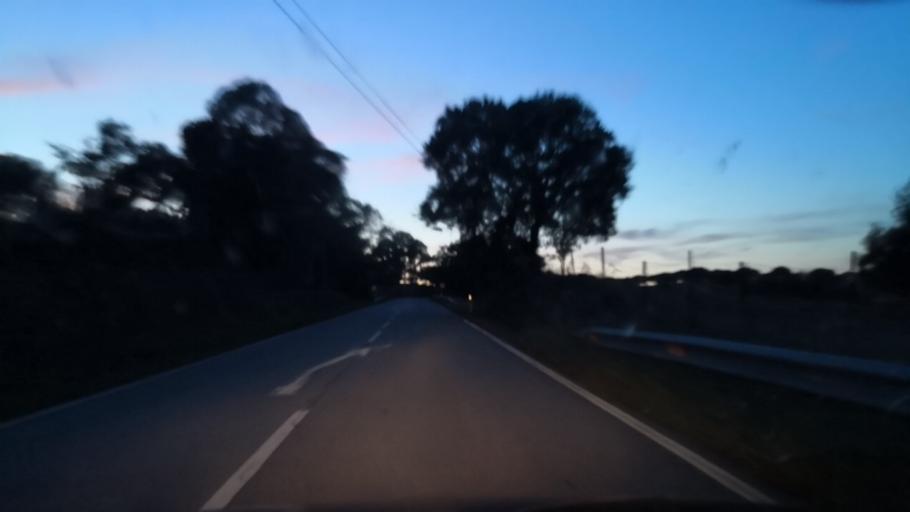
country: ES
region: Extremadura
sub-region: Provincia de Caceres
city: Piedras Albas
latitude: 39.8423
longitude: -6.9769
